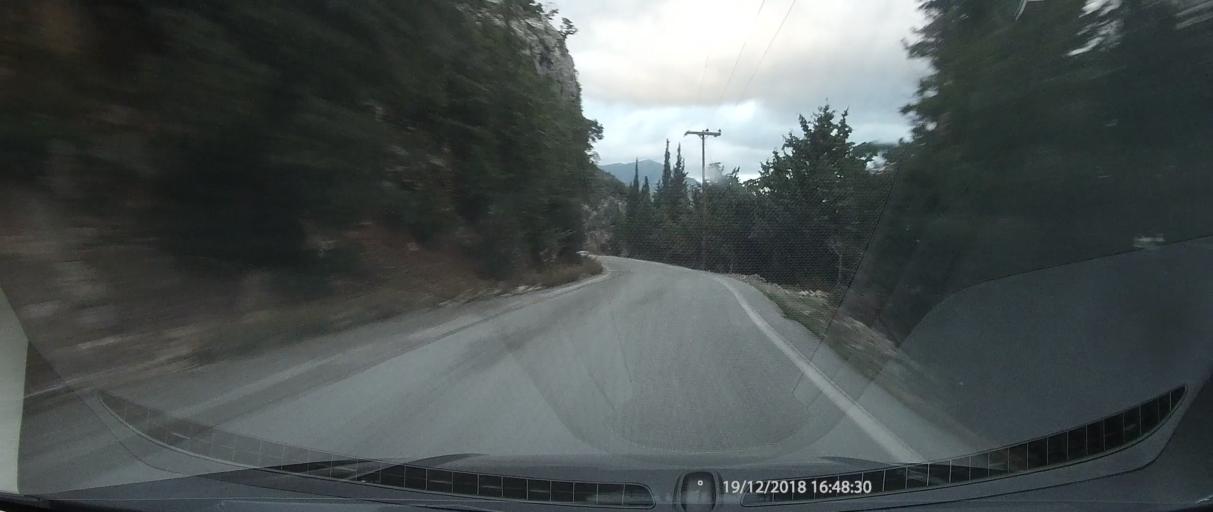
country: GR
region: Peloponnese
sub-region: Nomos Lakonias
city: Sykea
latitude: 36.9374
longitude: 22.9981
